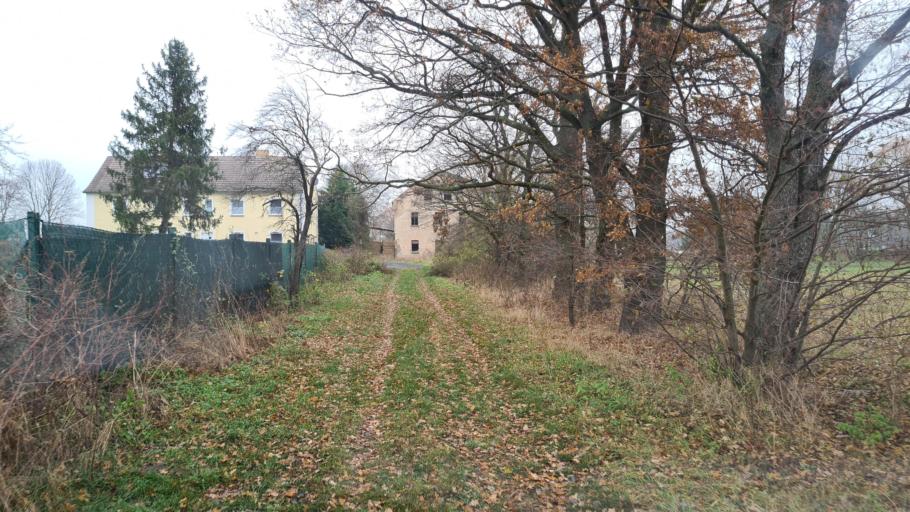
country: DE
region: Brandenburg
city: Schraden
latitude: 51.4187
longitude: 13.7133
